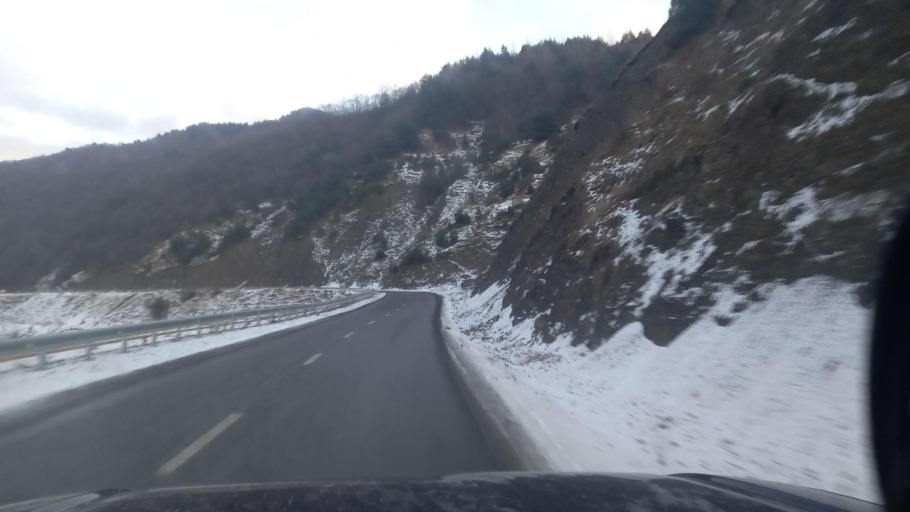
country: RU
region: Ingushetiya
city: Dzhayrakh
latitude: 42.8110
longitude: 44.8026
